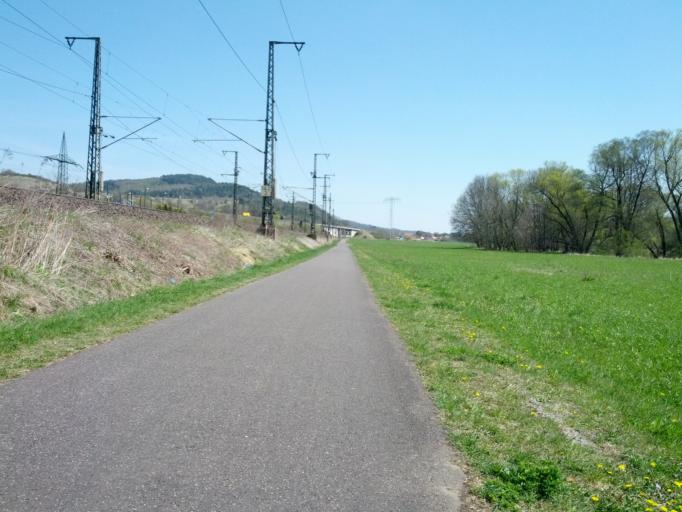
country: DE
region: Thuringia
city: Thal
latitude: 50.9642
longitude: 10.3695
